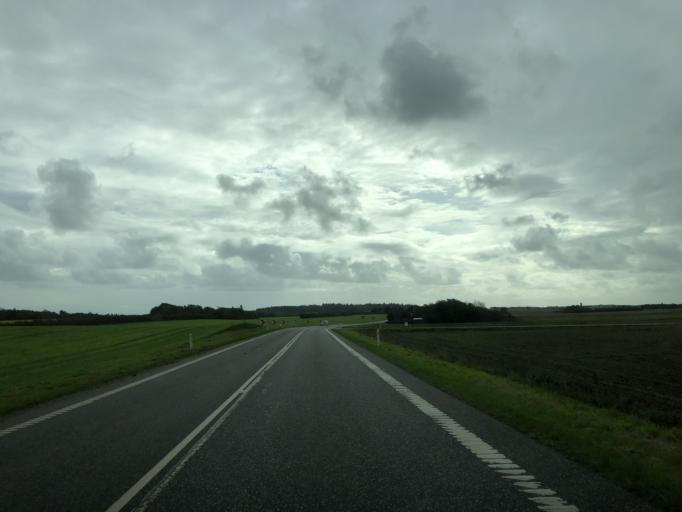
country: DK
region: North Denmark
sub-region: Thisted Kommune
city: Hurup
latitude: 56.7280
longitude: 8.4282
